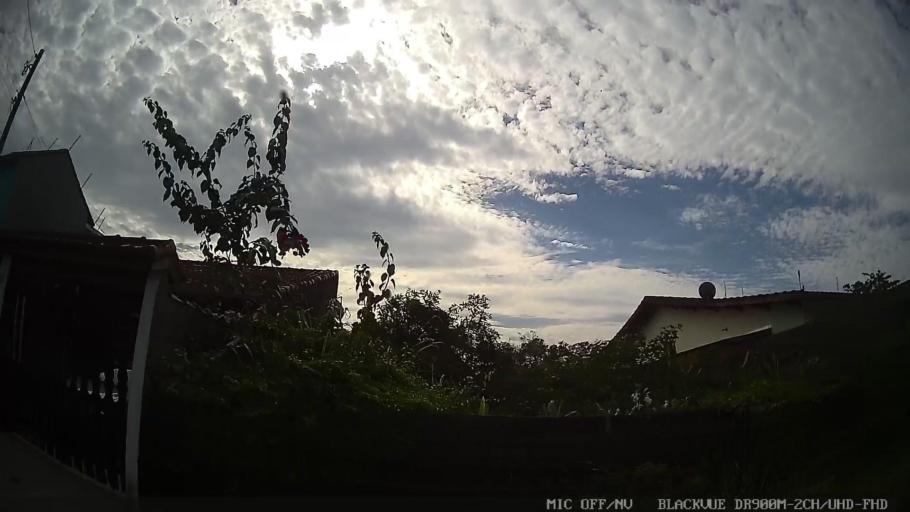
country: BR
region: Sao Paulo
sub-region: Itanhaem
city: Itanhaem
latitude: -24.1590
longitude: -46.7579
